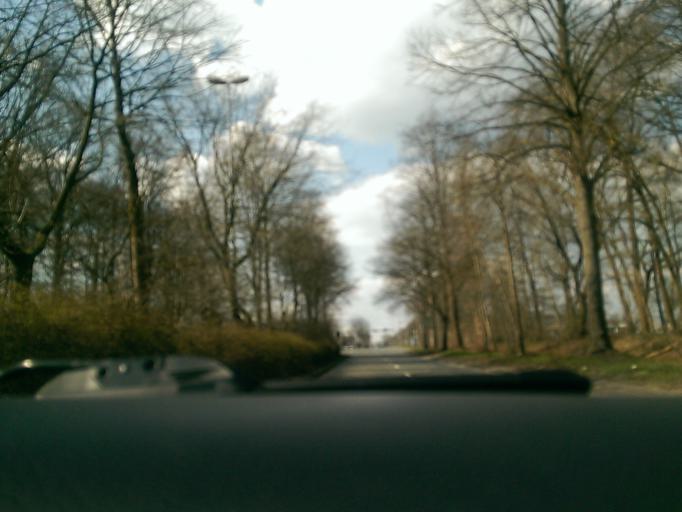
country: DE
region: North Rhine-Westphalia
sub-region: Regierungsbezirk Munster
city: Muenster
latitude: 51.9328
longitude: 7.6624
